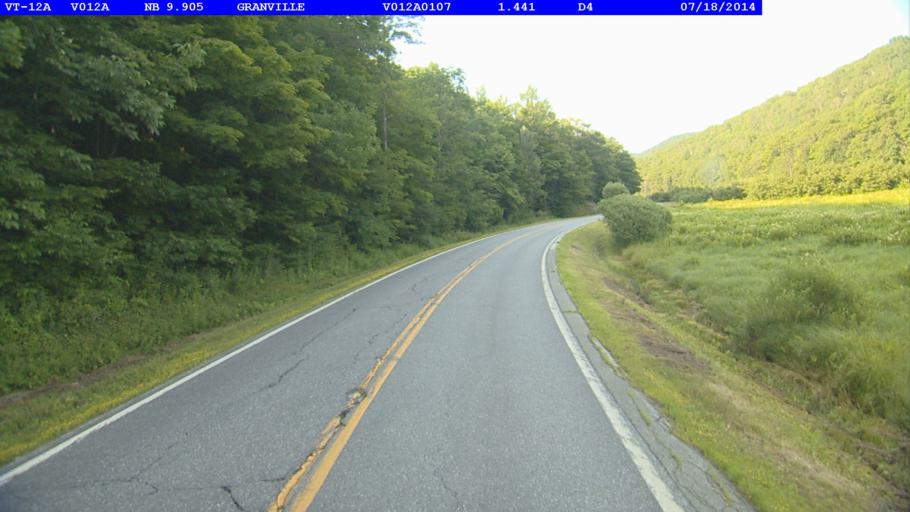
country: US
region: Vermont
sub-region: Orange County
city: Randolph
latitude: 44.0307
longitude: -72.7583
